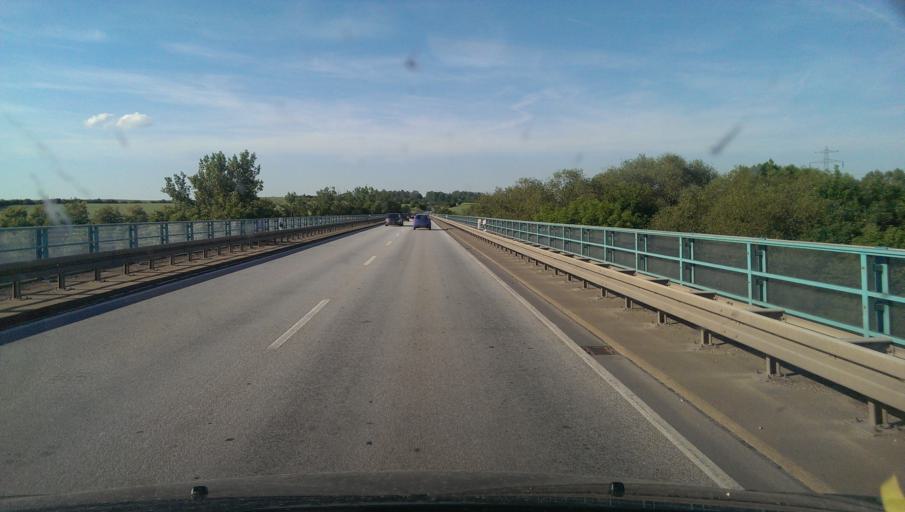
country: DE
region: Saxony-Anhalt
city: Theissen
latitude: 51.0566
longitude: 12.0988
